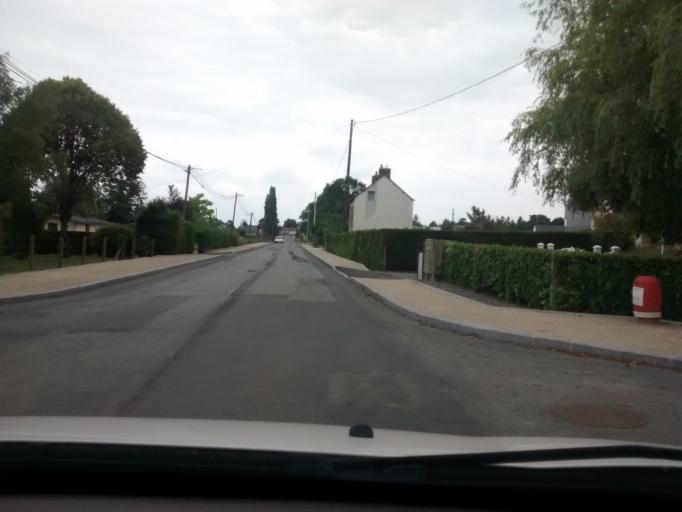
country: FR
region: Brittany
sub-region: Departement d'Ille-et-Vilaine
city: La Bouexiere
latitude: 48.1711
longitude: -1.4366
